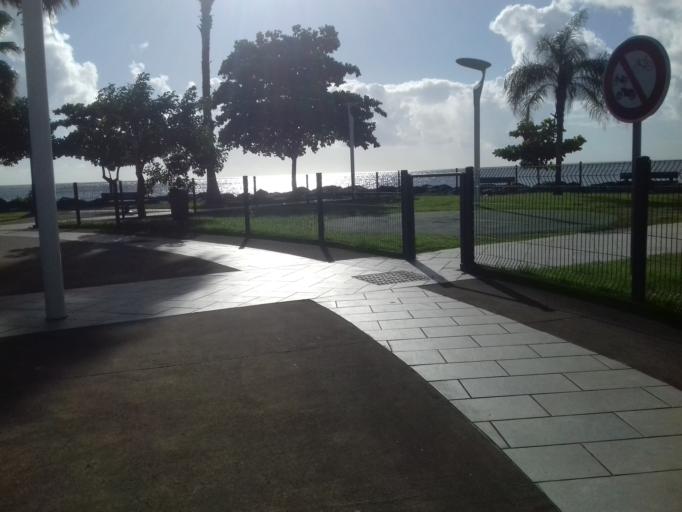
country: MQ
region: Martinique
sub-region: Martinique
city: Fort-de-France
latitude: 14.6167
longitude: -61.1040
